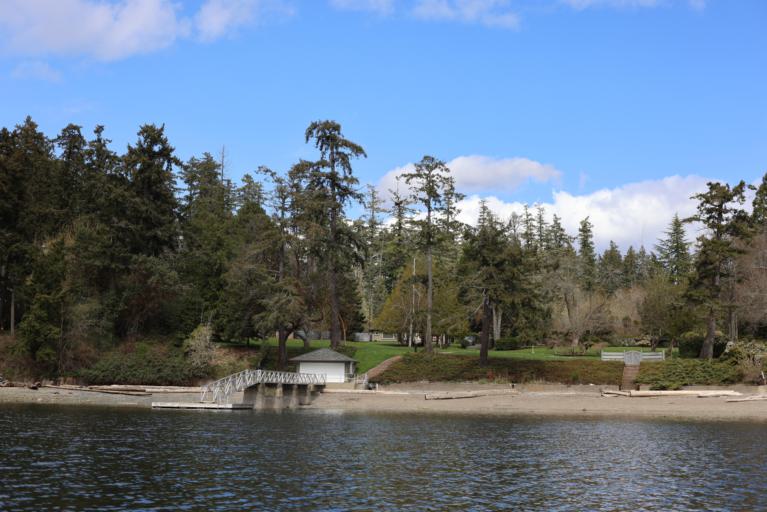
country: CA
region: British Columbia
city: North Saanich
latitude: 48.6278
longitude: -123.4749
